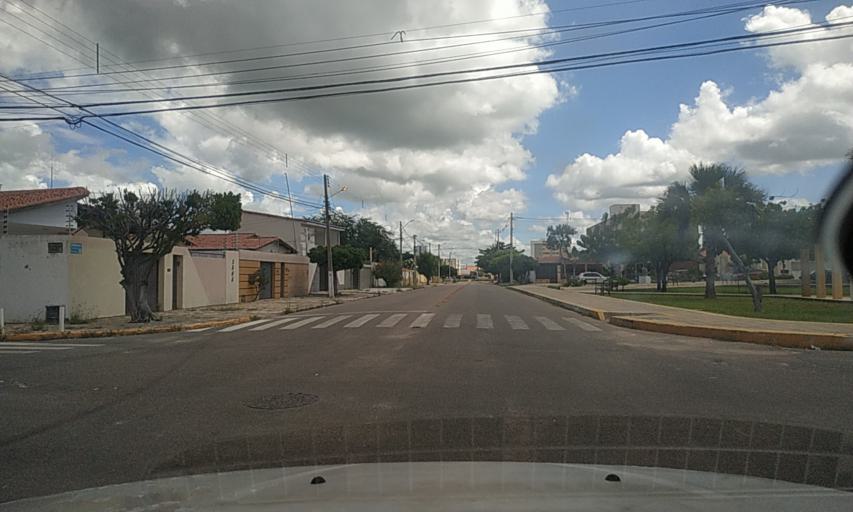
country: BR
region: Rio Grande do Norte
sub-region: Mossoro
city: Mossoro
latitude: -5.1783
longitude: -37.3632
